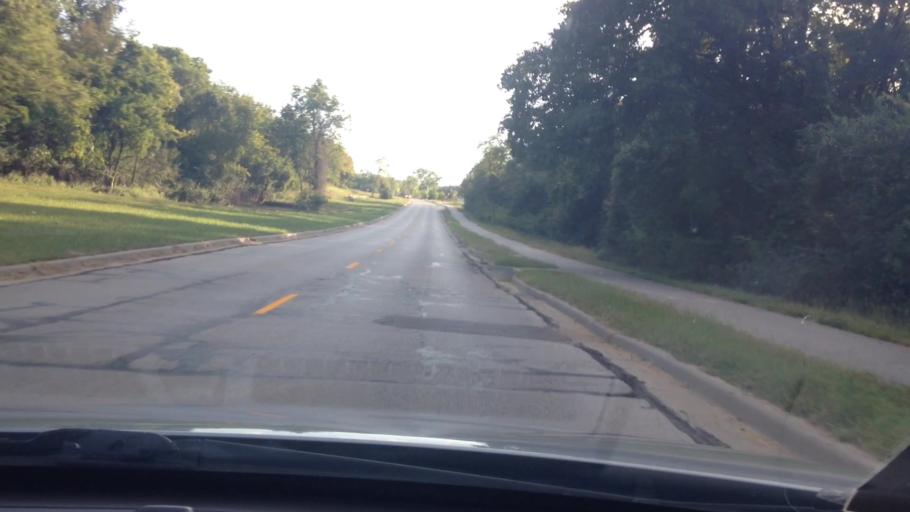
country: US
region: Missouri
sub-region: Jackson County
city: Grandview
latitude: 38.9002
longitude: -94.5181
